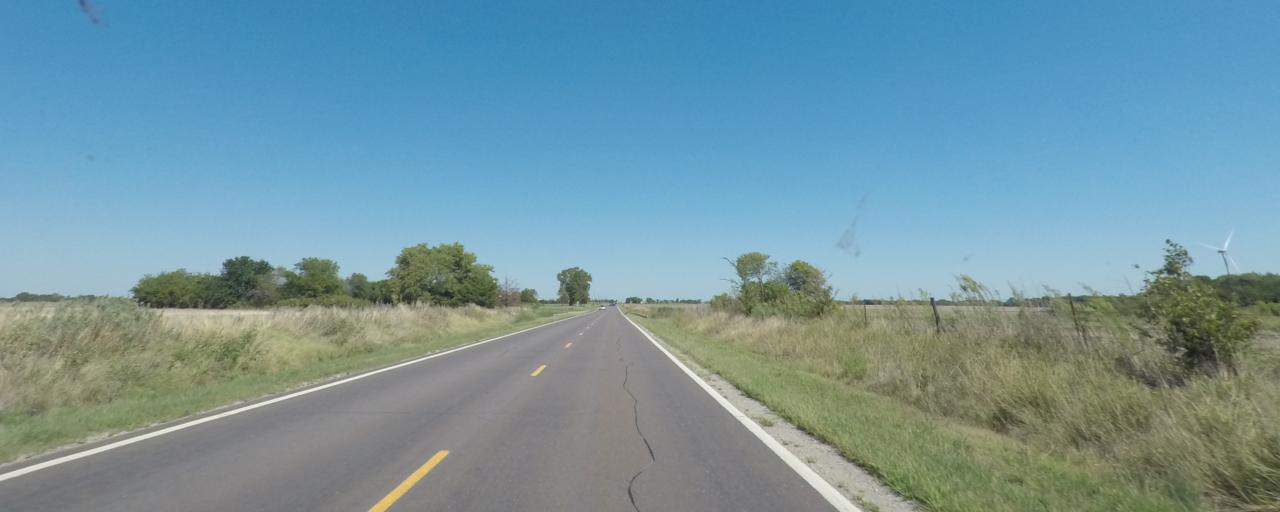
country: US
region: Kansas
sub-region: Sumner County
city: Wellington
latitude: 37.1358
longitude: -97.4020
